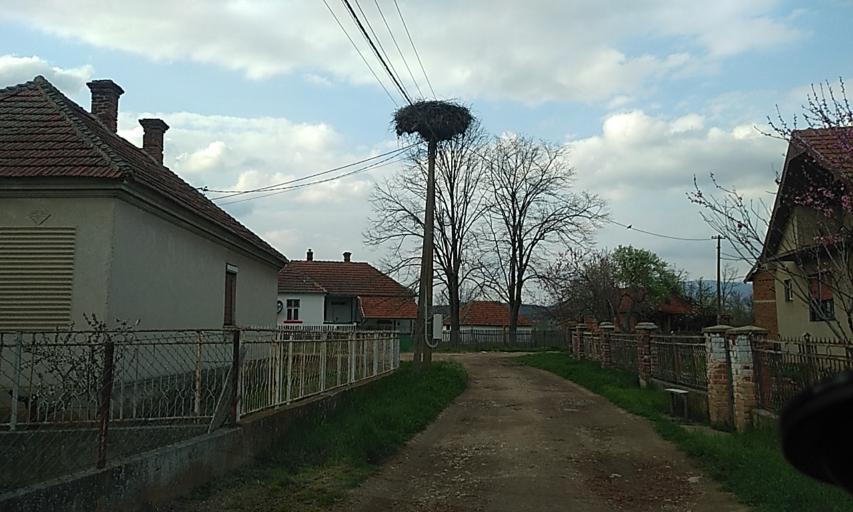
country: RS
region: Central Serbia
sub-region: Nisavski Okrug
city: Razanj
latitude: 43.5948
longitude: 21.6079
